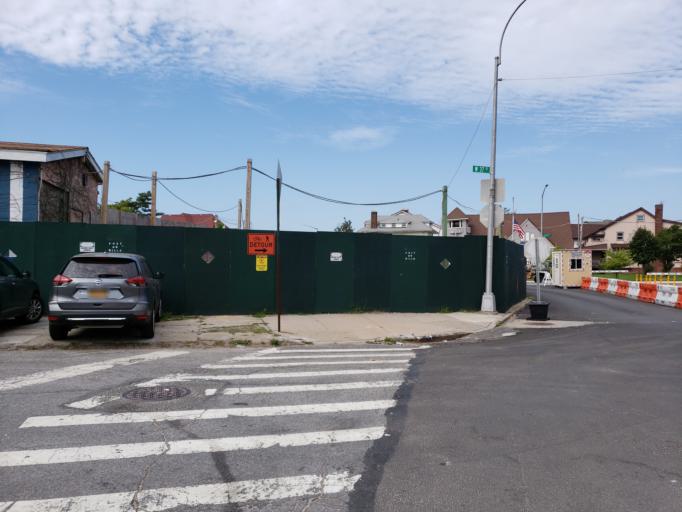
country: US
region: New York
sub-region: Kings County
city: Coney Island
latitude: 40.5732
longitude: -74.0025
